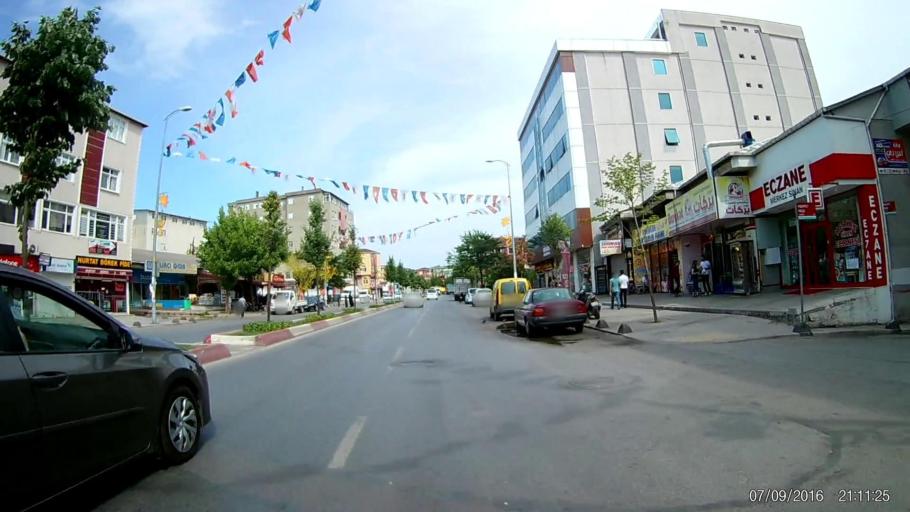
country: TR
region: Istanbul
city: Sultanbeyli
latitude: 40.9645
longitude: 29.2793
